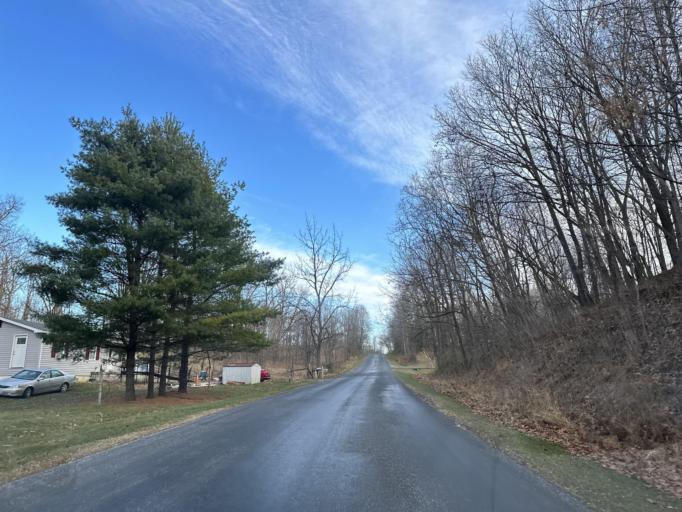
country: US
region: Virginia
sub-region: City of Staunton
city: Staunton
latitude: 38.2255
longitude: -79.2119
